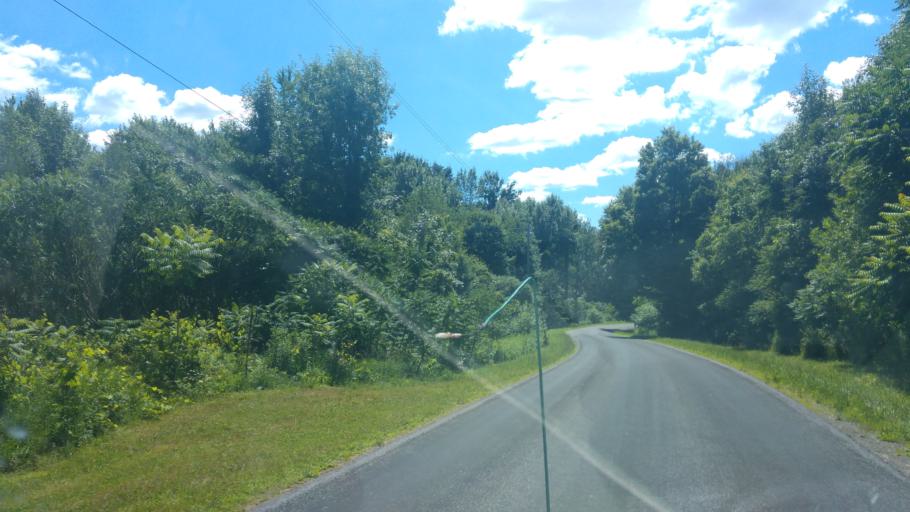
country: US
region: New York
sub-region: Wayne County
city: Lyons
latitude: 43.1488
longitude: -76.9661
